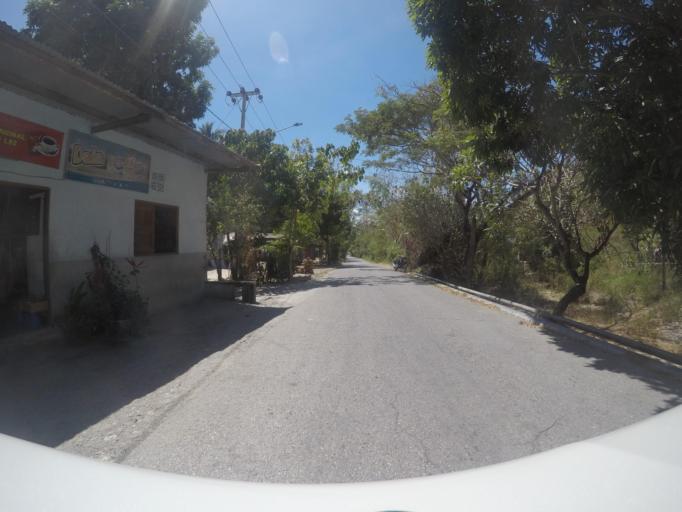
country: TL
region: Baucau
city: Baucau
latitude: -8.4621
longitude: 126.4432
